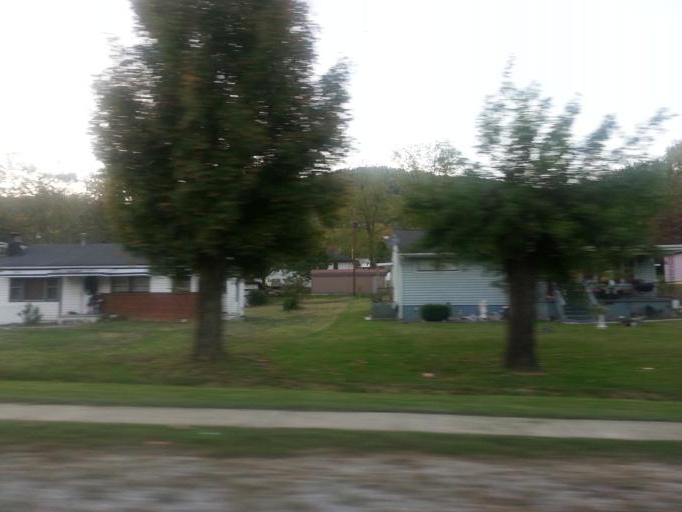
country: US
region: Tennessee
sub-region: Campbell County
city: Hunter
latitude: 36.3716
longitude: -84.1340
